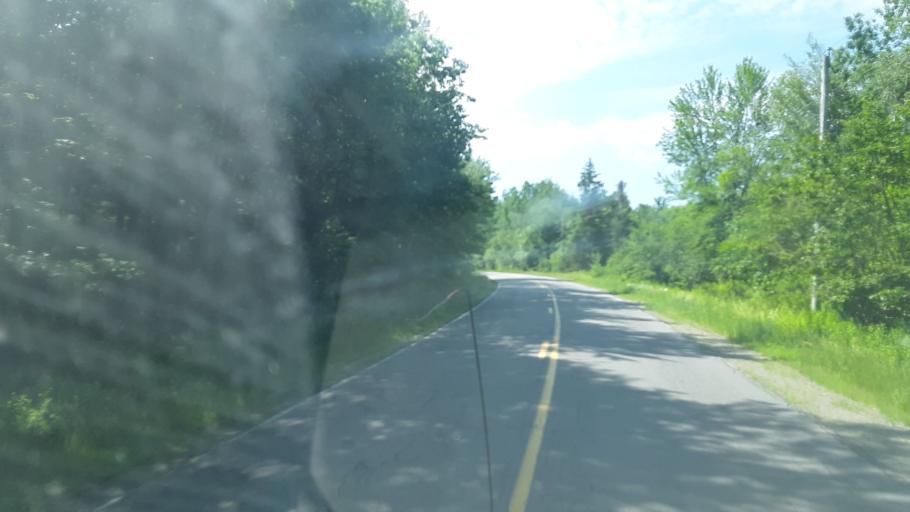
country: US
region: Maine
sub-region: Waldo County
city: Swanville
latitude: 44.5618
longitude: -68.9542
